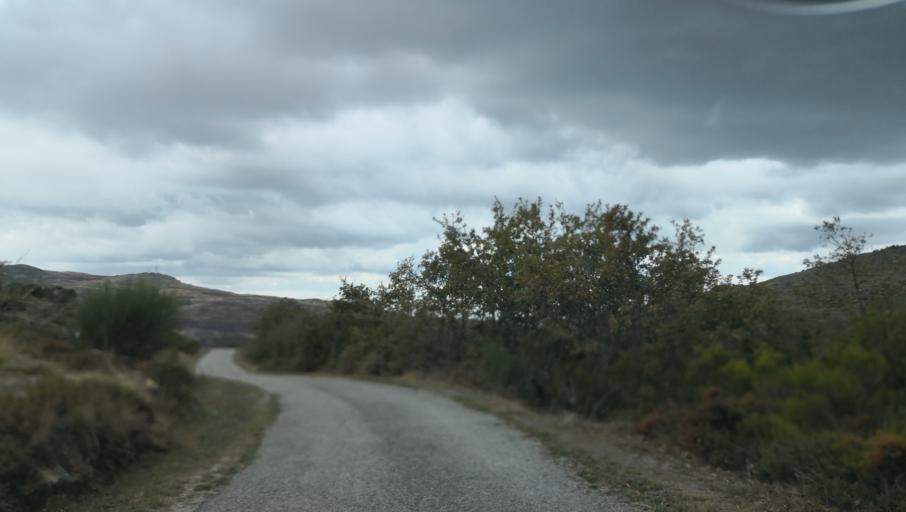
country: PT
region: Vila Real
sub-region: Vila Real
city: Vila Real
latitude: 41.3827
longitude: -7.8080
